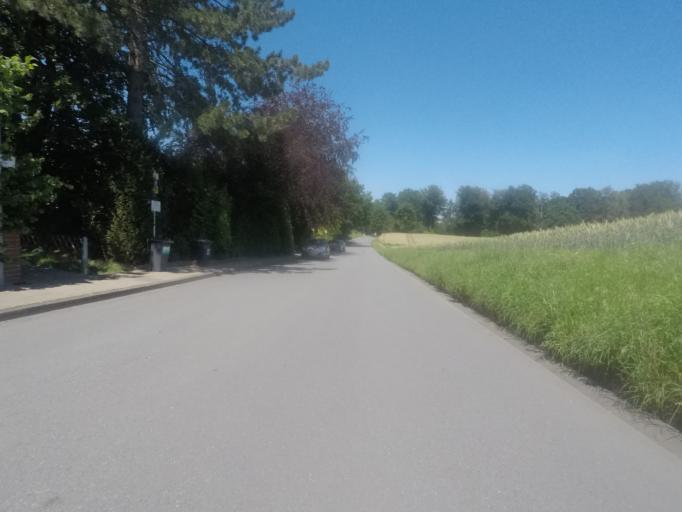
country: DE
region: North Rhine-Westphalia
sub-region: Regierungsbezirk Detmold
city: Bielefeld
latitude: 52.0728
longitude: 8.5202
